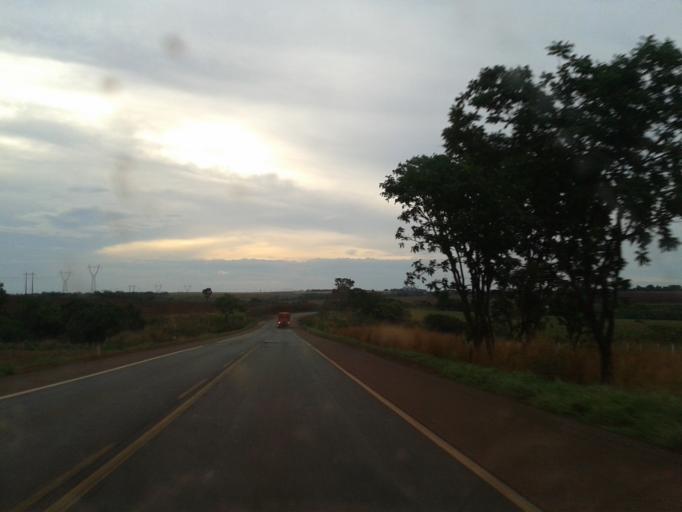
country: BR
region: Goias
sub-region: Santa Helena De Goias
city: Santa Helena de Goias
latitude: -17.9559
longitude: -50.5049
